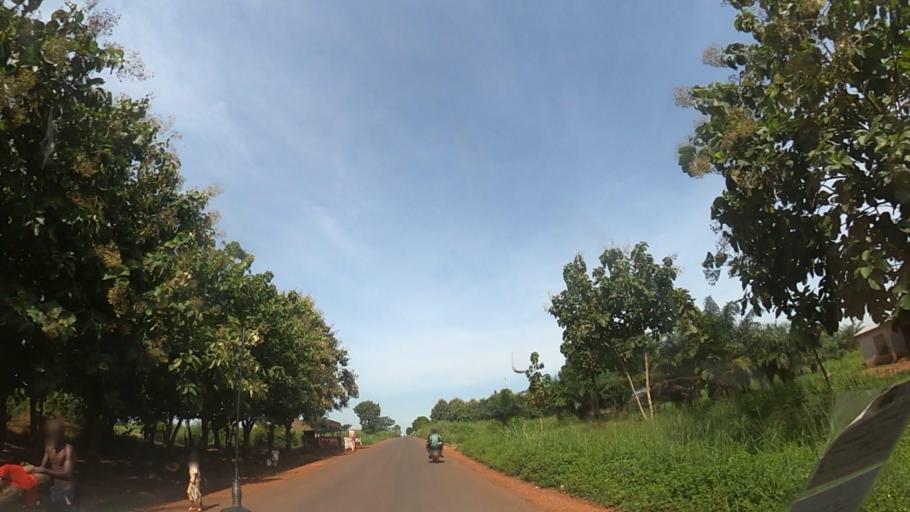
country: CF
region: Ombella-Mpoko
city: Bimbo
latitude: 4.3130
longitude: 18.4751
